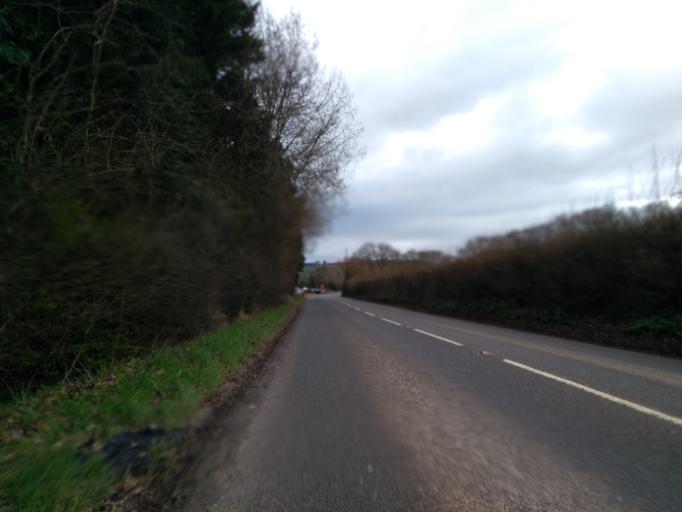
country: GB
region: England
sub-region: Devon
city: Heavitree
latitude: 50.7984
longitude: -3.4975
